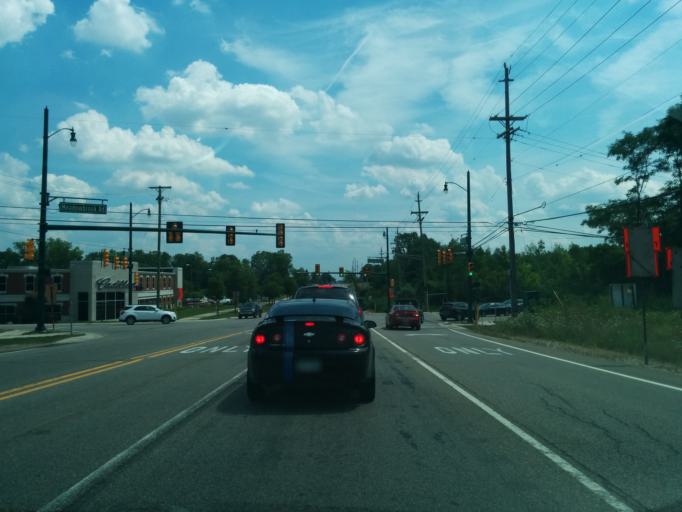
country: US
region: Michigan
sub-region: Oakland County
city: Novi
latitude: 42.4765
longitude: -83.4565
